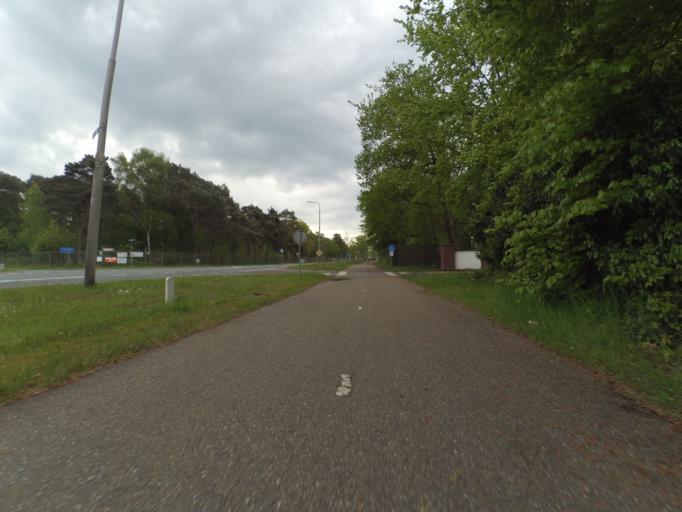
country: NL
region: Utrecht
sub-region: Gemeente Soest
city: Soest
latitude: 52.1235
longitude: 5.3018
